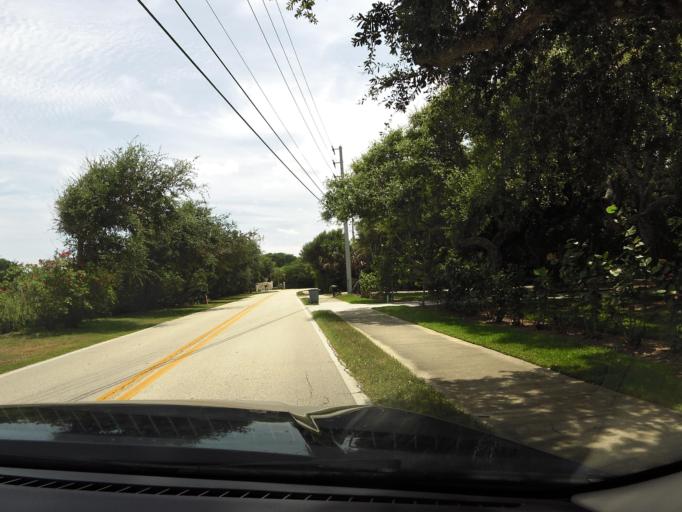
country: US
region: Florida
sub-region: Volusia County
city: Ponce Inlet
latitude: 29.0886
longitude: -80.9348
